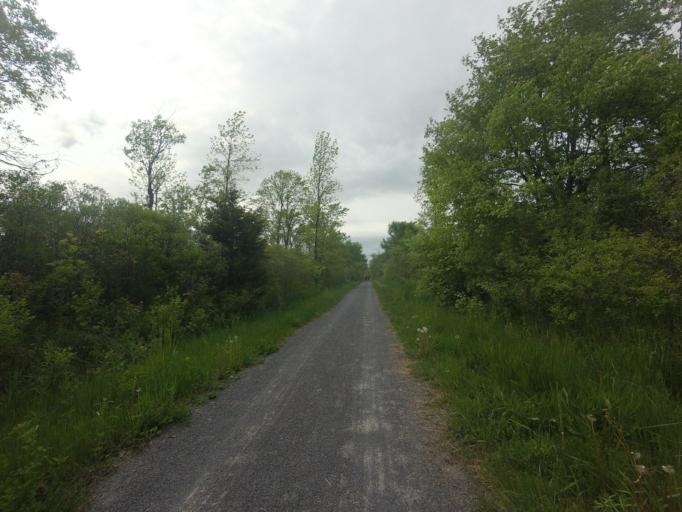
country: CA
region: Ontario
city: Kingston
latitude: 44.3519
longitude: -76.6163
